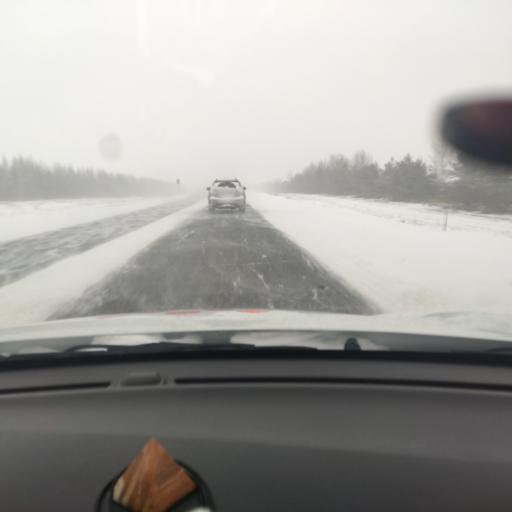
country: RU
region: Tatarstan
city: Verkhniy Uslon
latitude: 55.6663
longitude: 48.8633
